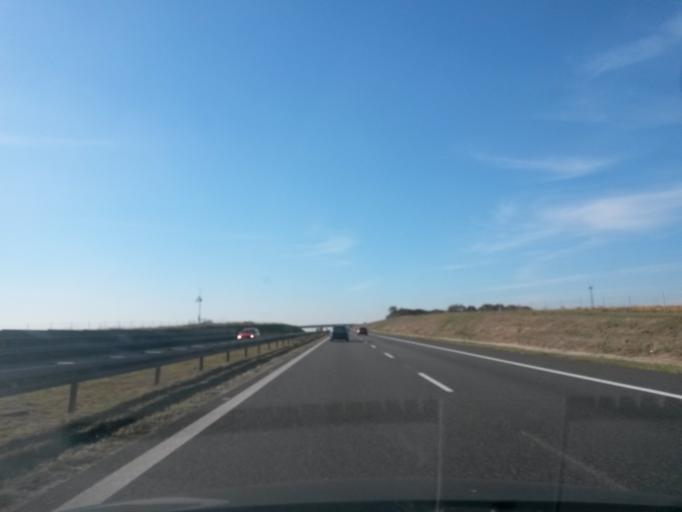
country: PL
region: Opole Voivodeship
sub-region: Powiat krapkowicki
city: Gogolin
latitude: 50.4808
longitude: 18.0586
